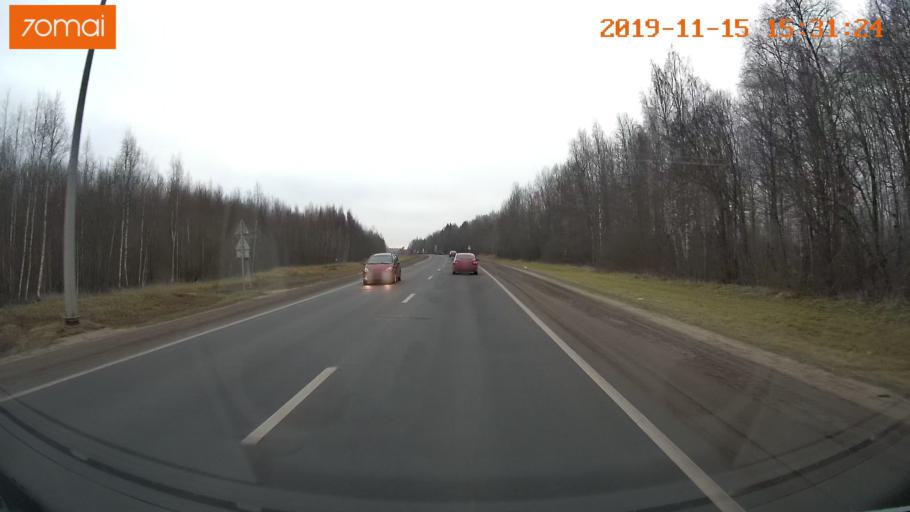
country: RU
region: Jaroslavl
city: Danilov
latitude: 58.1007
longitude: 40.1076
